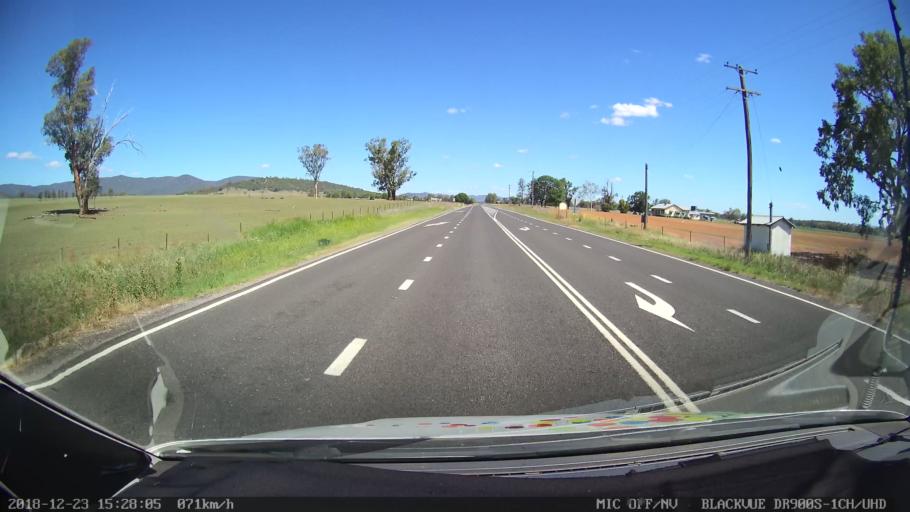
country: AU
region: New South Wales
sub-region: Tamworth Municipality
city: East Tamworth
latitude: -30.9328
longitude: 150.8496
